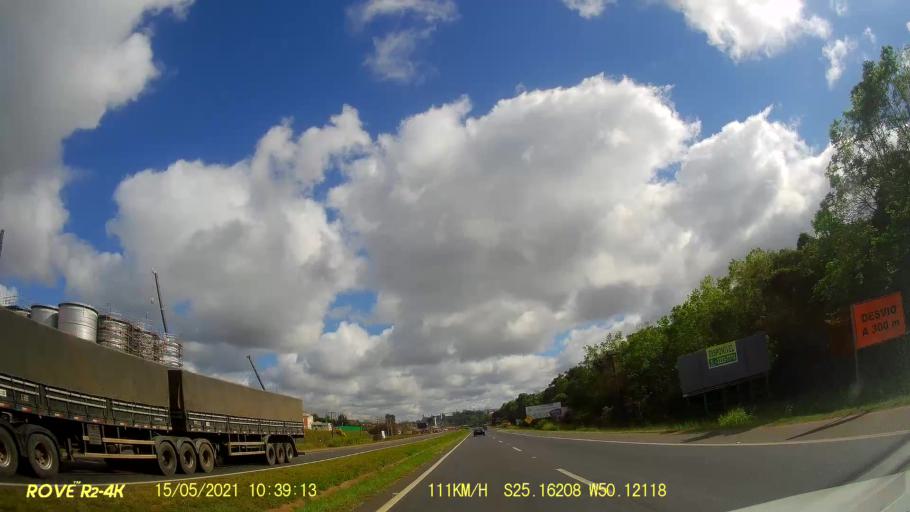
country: BR
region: Parana
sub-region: Ponta Grossa
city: Ponta Grossa
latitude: -25.1621
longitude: -50.1212
